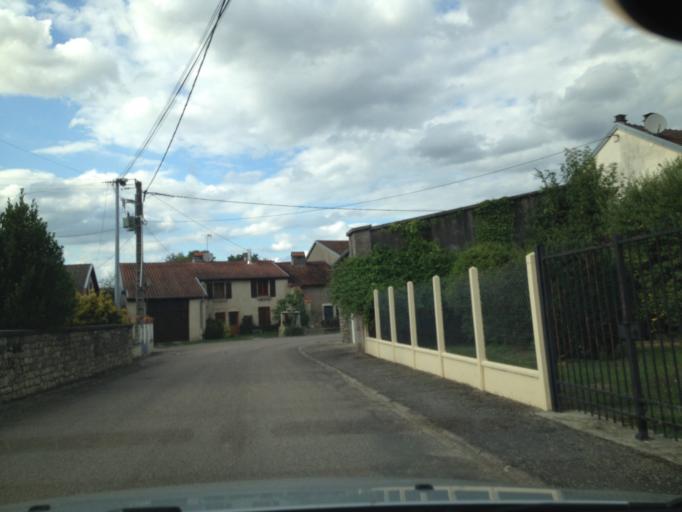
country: FR
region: Franche-Comte
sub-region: Departement de la Haute-Saone
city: Jussey
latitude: 47.8891
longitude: 5.9756
